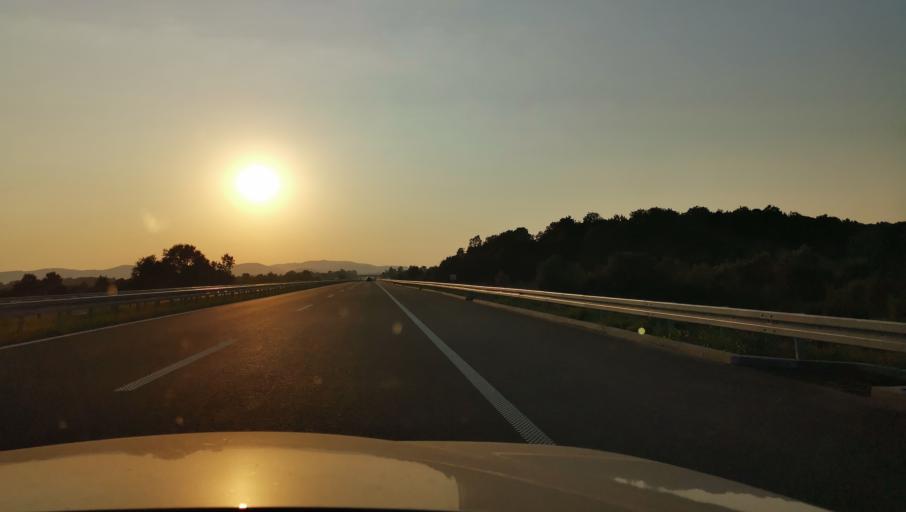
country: RS
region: Central Serbia
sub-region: Kolubarski Okrug
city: Lajkovac
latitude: 44.3490
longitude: 20.1650
